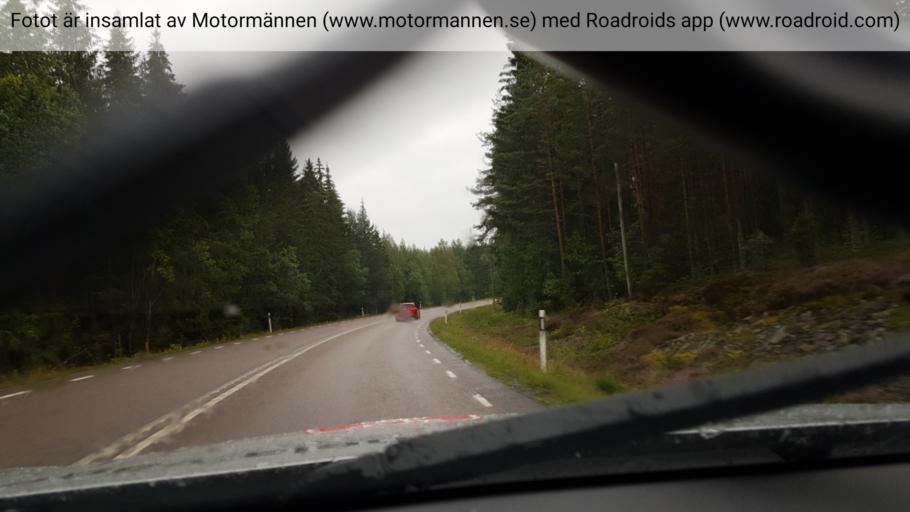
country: SE
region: Vaestra Goetaland
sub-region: Amals Kommun
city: Amal
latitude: 59.0720
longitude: 12.6508
